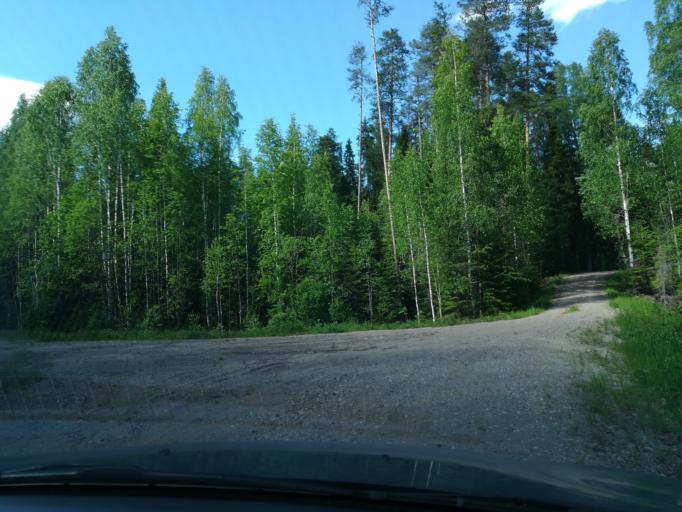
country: FI
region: South Karelia
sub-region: Imatra
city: Ruokolahti
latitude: 61.5494
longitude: 28.8115
